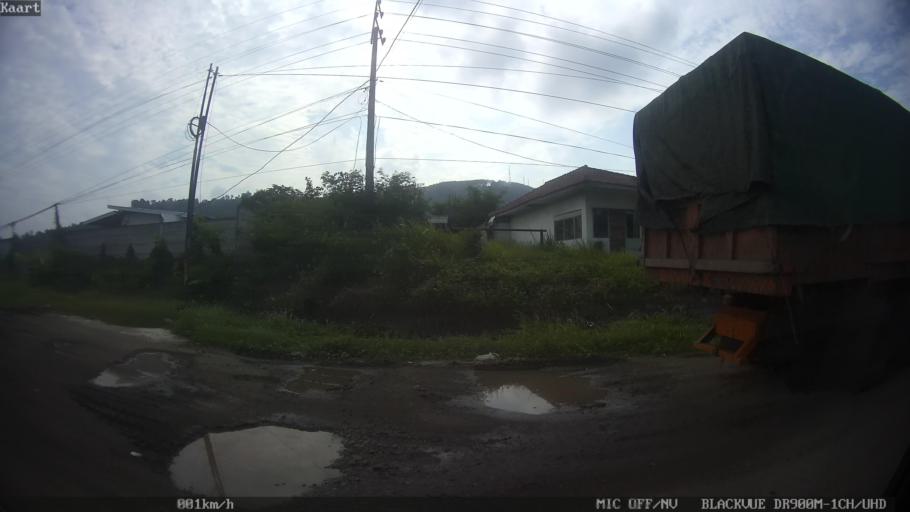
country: ID
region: Lampung
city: Bandarlampung
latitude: -5.4284
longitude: 105.2964
